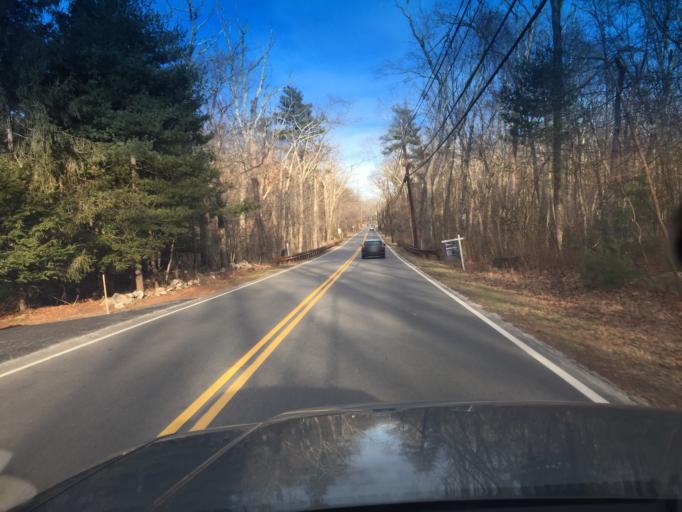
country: US
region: Massachusetts
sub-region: Middlesex County
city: Sherborn
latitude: 42.2293
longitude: -71.3874
